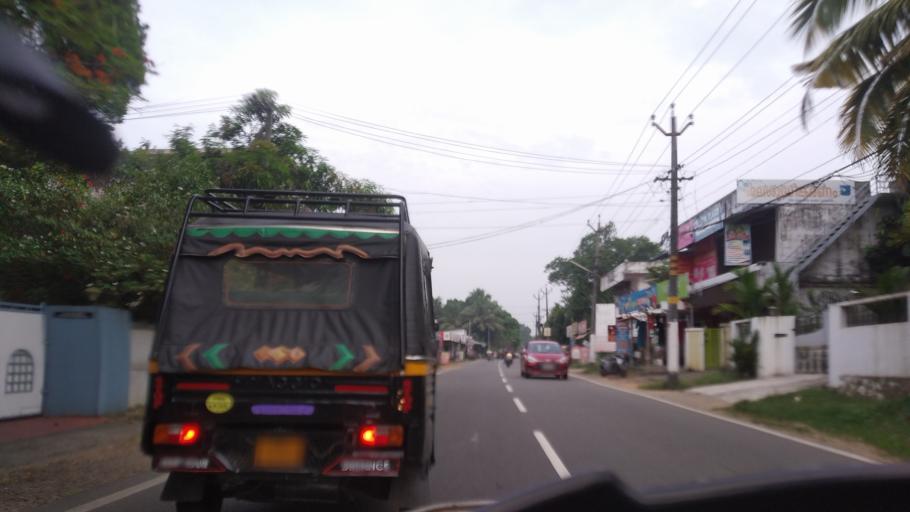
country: IN
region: Kerala
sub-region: Ernakulam
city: Elur
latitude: 10.1489
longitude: 76.2495
